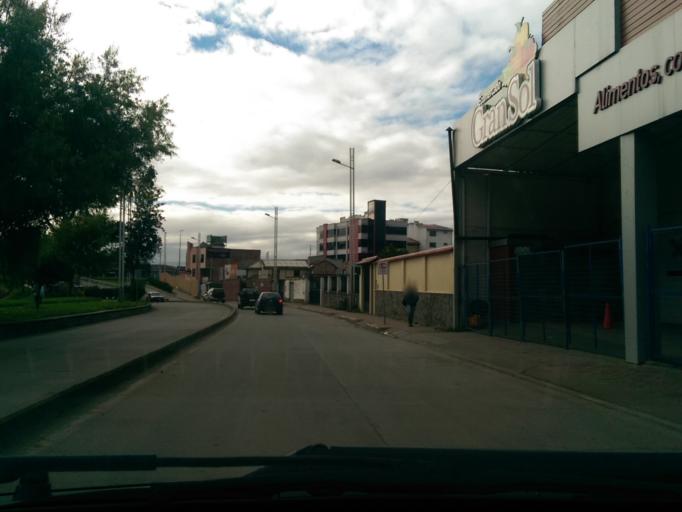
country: EC
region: Azuay
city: Cuenca
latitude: -2.8942
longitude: -79.0265
